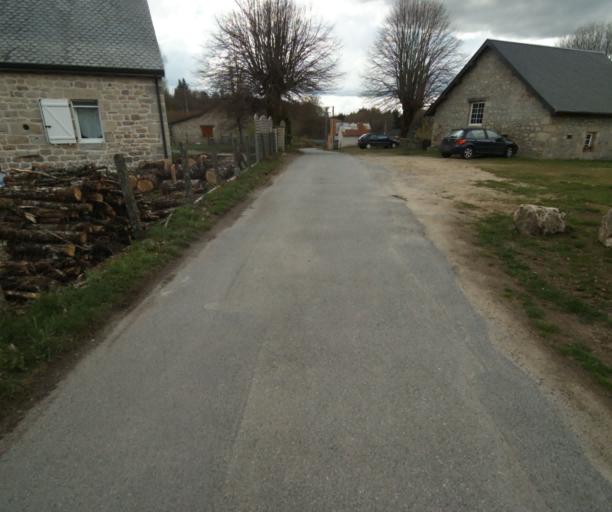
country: FR
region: Limousin
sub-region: Departement de la Correze
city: Correze
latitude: 45.2952
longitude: 1.9222
